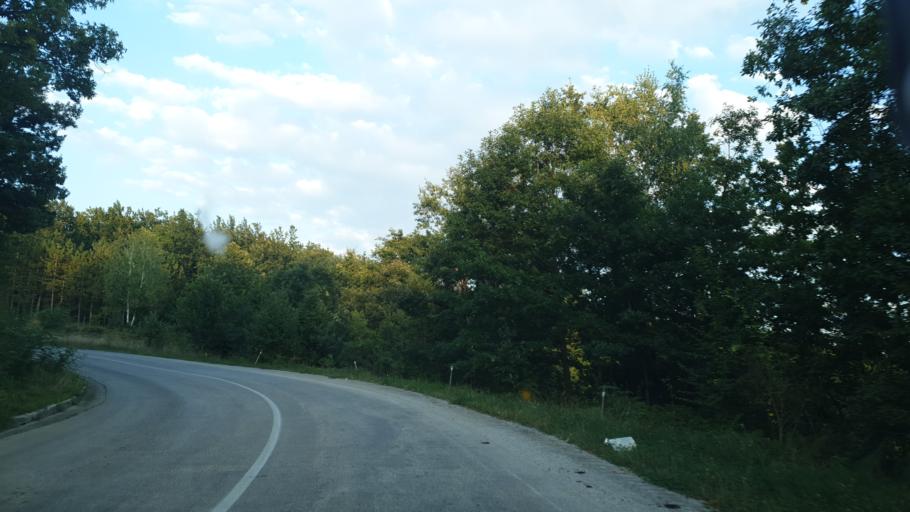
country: RS
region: Central Serbia
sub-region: Zlatiborski Okrug
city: Kosjeric
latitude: 44.0314
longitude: 20.0127
